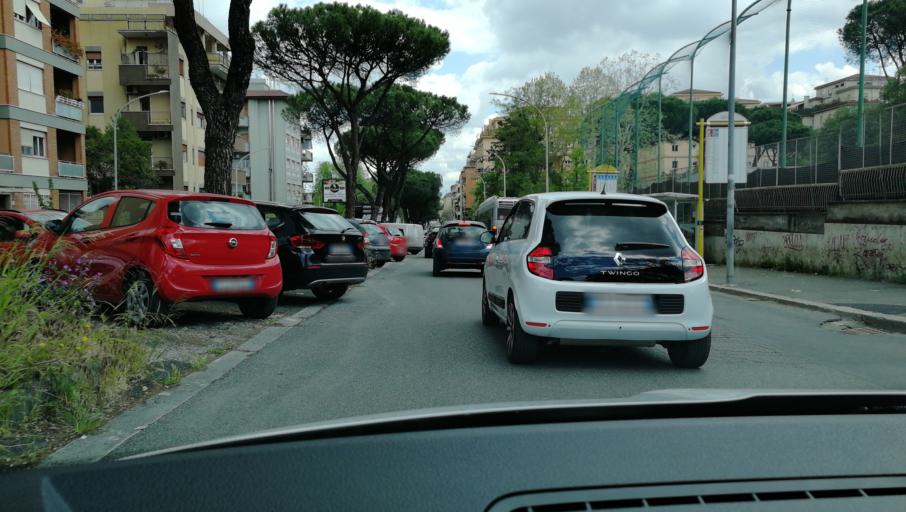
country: IT
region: Latium
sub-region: Citta metropolitana di Roma Capitale
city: Rome
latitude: 41.8476
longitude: 12.4880
